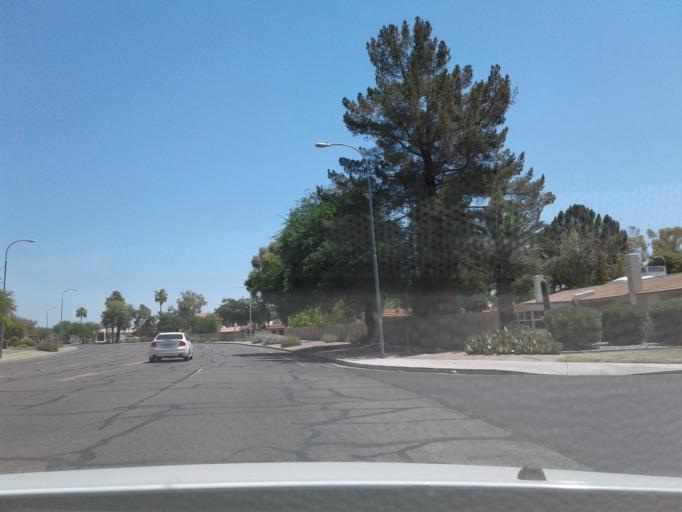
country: US
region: Arizona
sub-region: Maricopa County
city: Guadalupe
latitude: 33.3444
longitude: -111.9813
